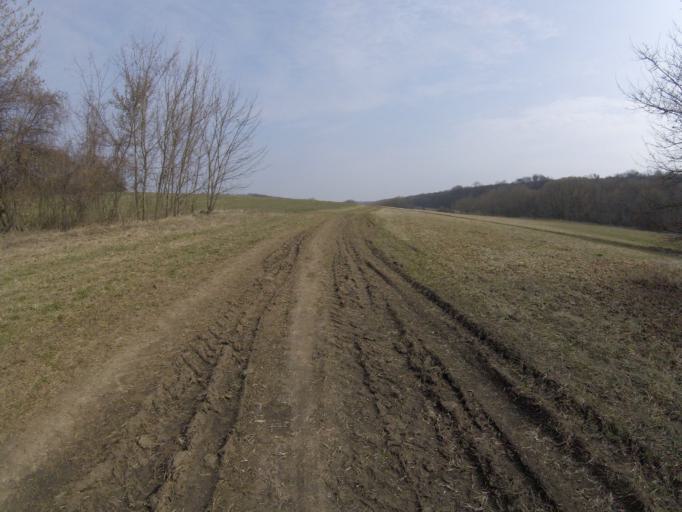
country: HU
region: Pest
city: Hevizgyoerk
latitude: 47.5996
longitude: 19.5042
